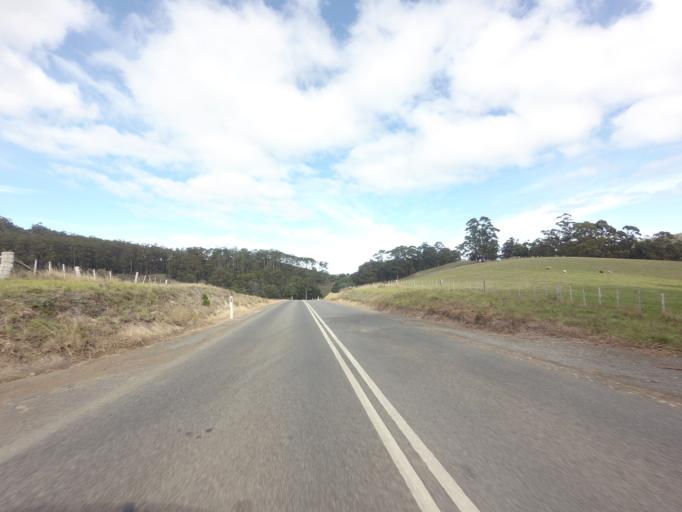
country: AU
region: Tasmania
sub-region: Clarence
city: Sandford
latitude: -43.0754
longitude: 147.7494
